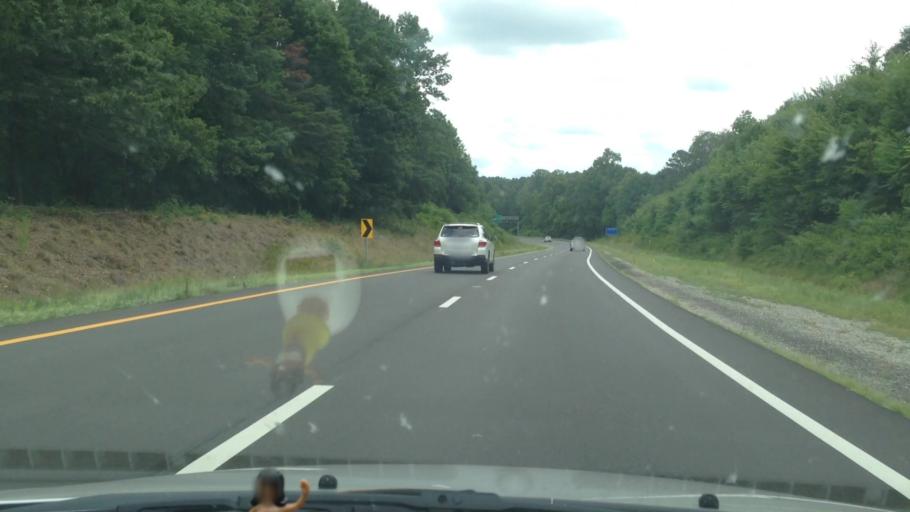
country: US
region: Virginia
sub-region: Pittsylvania County
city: Gretna
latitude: 36.9222
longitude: -79.3805
